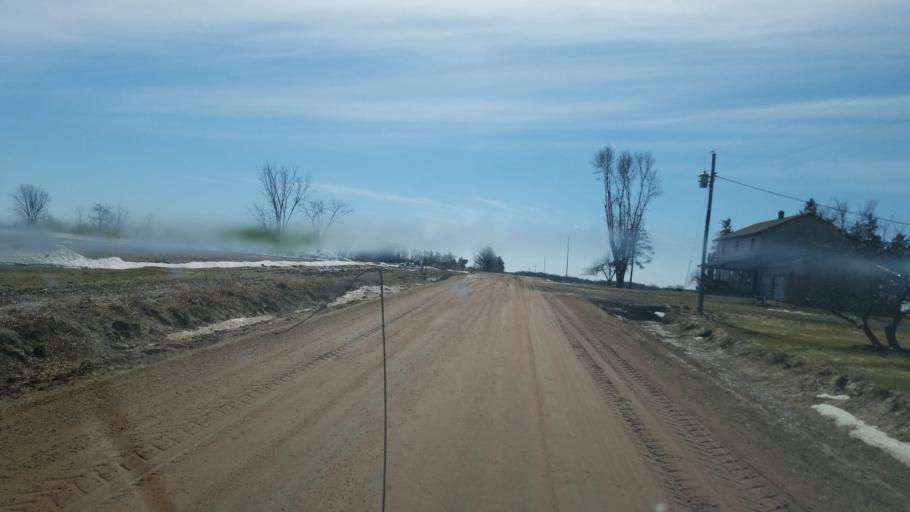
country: US
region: Wisconsin
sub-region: Clark County
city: Loyal
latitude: 44.6157
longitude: -90.4273
